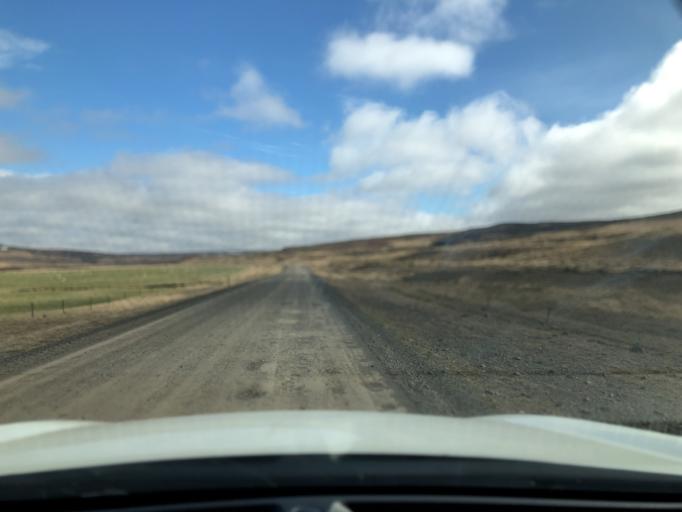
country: IS
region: West
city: Borgarnes
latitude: 65.1878
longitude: -21.4703
